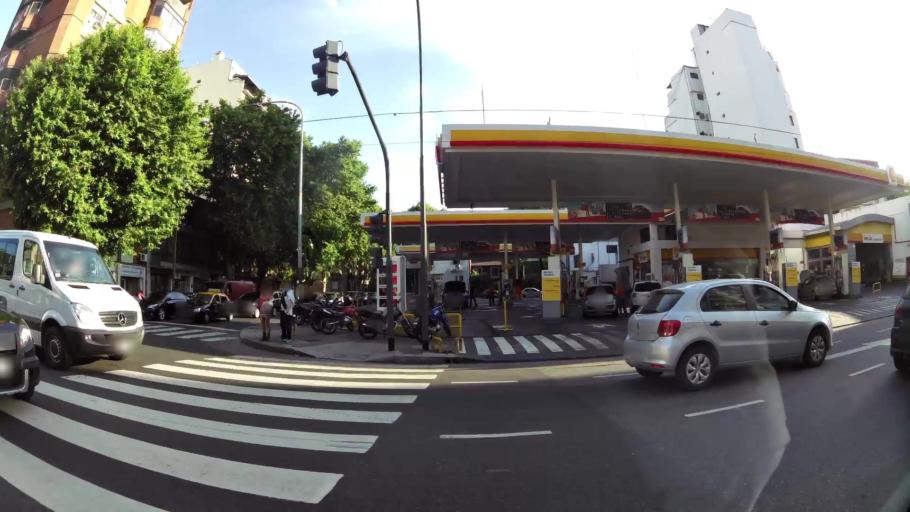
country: AR
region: Buenos Aires F.D.
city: Colegiales
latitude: -34.5978
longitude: -58.4192
